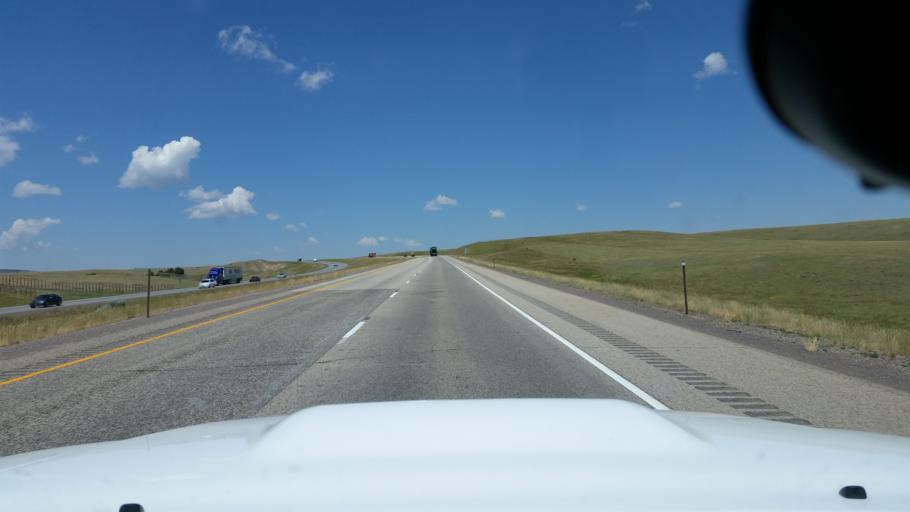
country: US
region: Wyoming
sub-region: Albany County
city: Laramie
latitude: 41.4585
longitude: -105.9788
